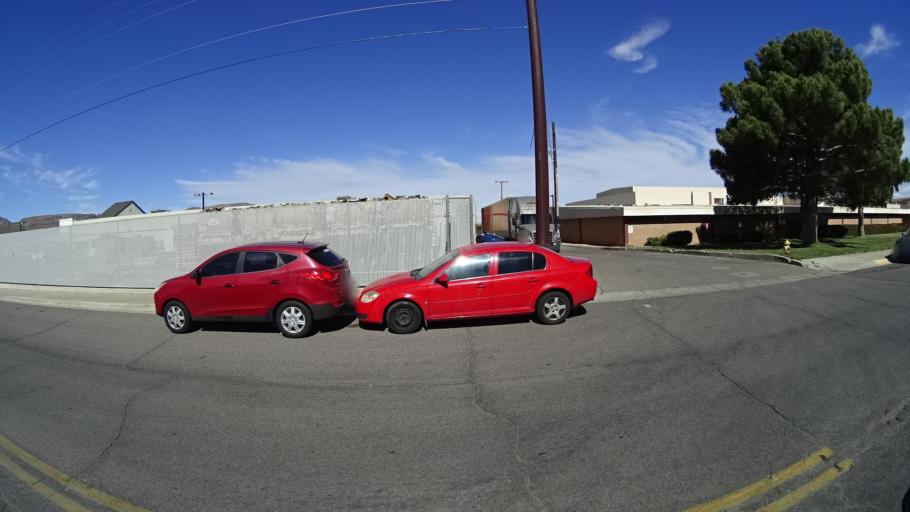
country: US
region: Arizona
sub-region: Mohave County
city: Kingman
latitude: 35.2140
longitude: -114.0337
